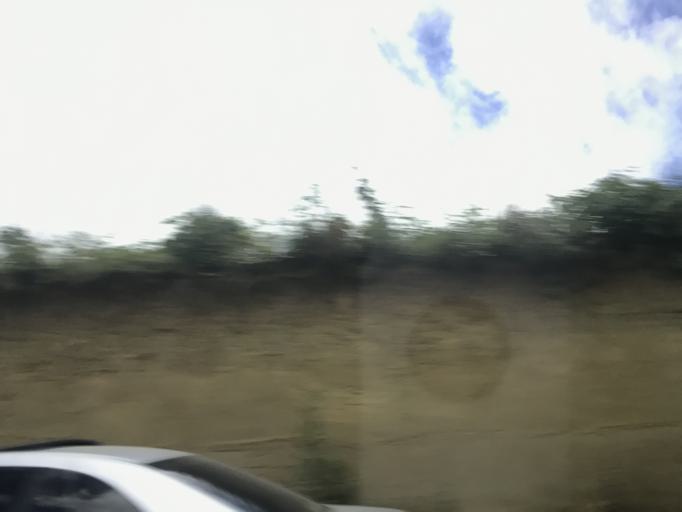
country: GT
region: Chimaltenango
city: Parramos
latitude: 14.6268
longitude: -90.8076
